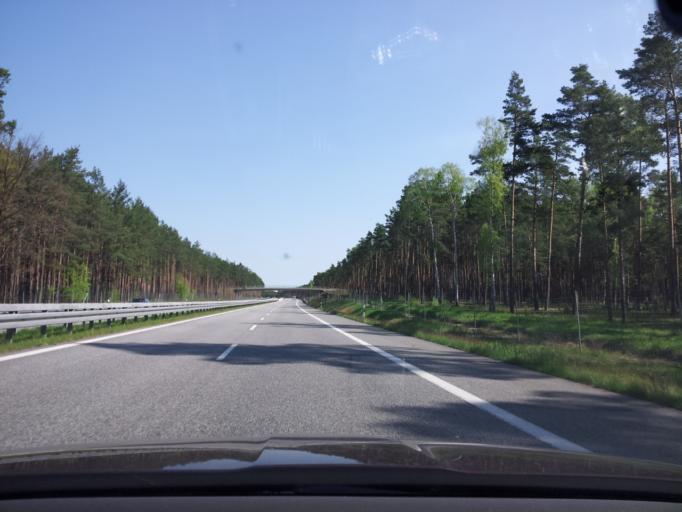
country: DE
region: Brandenburg
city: Trebbin
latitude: 52.1433
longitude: 13.2329
